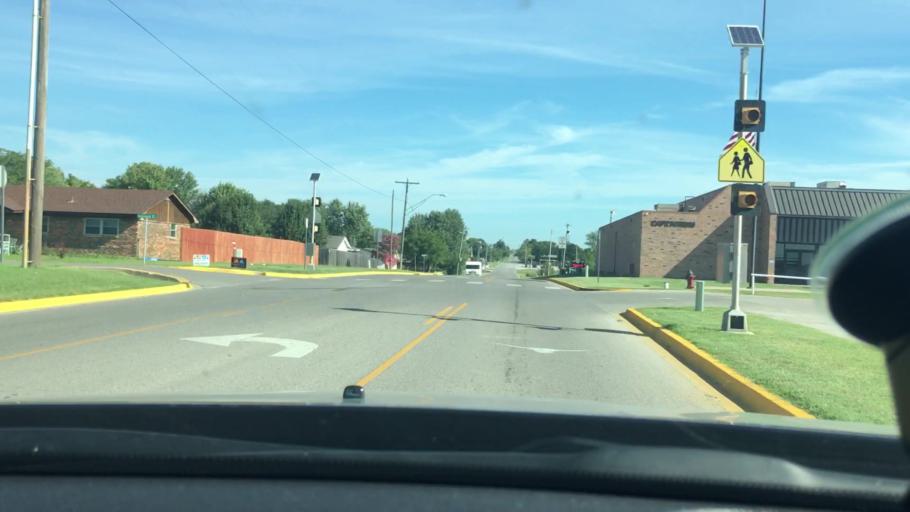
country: US
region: Oklahoma
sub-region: Carter County
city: Lone Grove
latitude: 34.1776
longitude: -97.2474
